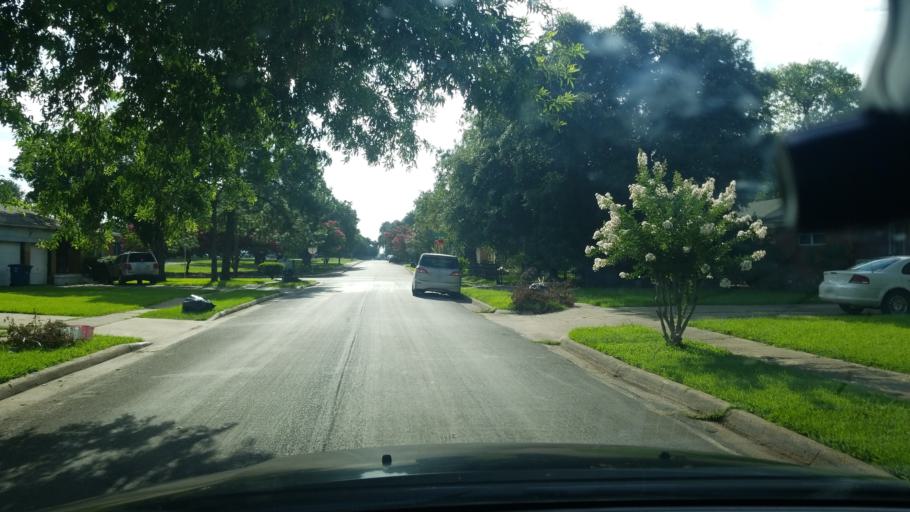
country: US
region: Texas
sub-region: Dallas County
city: Balch Springs
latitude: 32.7507
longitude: -96.6749
